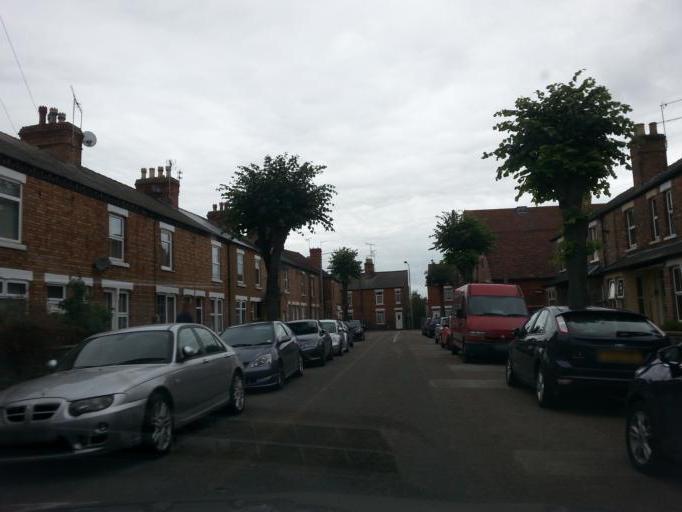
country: GB
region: England
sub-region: Nottinghamshire
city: Newark on Trent
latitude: 53.0721
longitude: -0.7976
